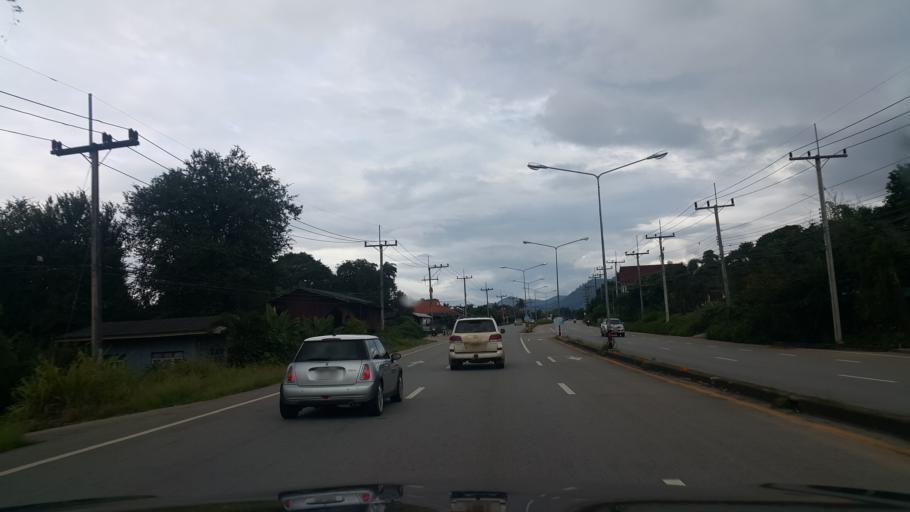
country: TH
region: Lampang
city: Wang Nuea
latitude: 19.1556
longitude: 99.5008
